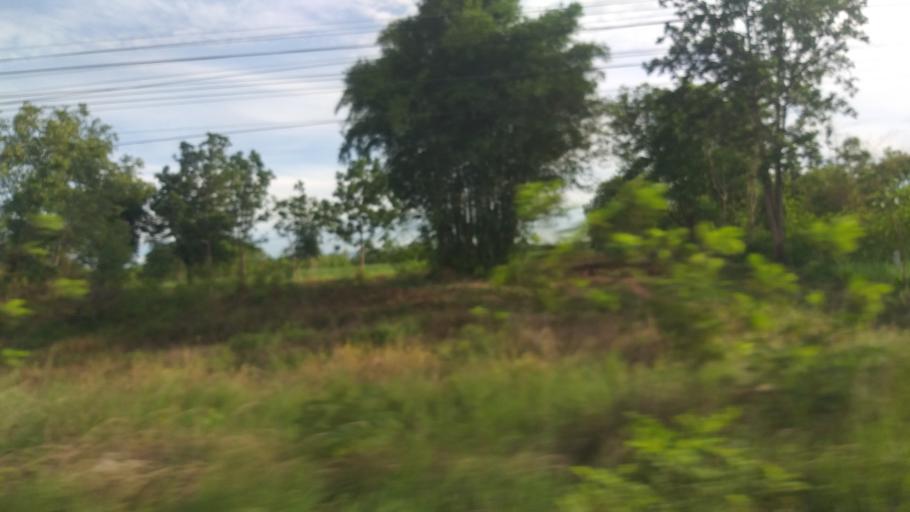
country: TH
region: Chaiyaphum
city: Ban Thaen
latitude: 16.3779
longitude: 102.2846
